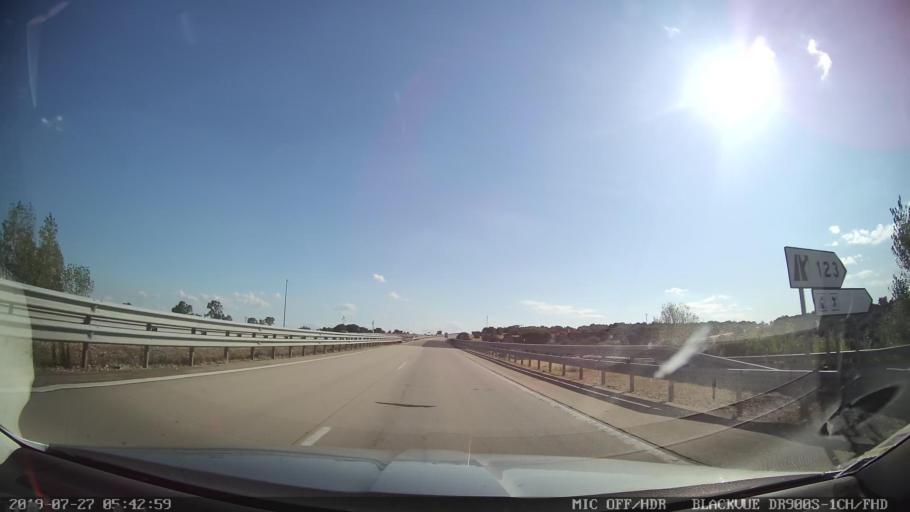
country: ES
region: Castille-La Mancha
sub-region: Province of Toledo
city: Mejorada
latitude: 39.9618
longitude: -4.9030
